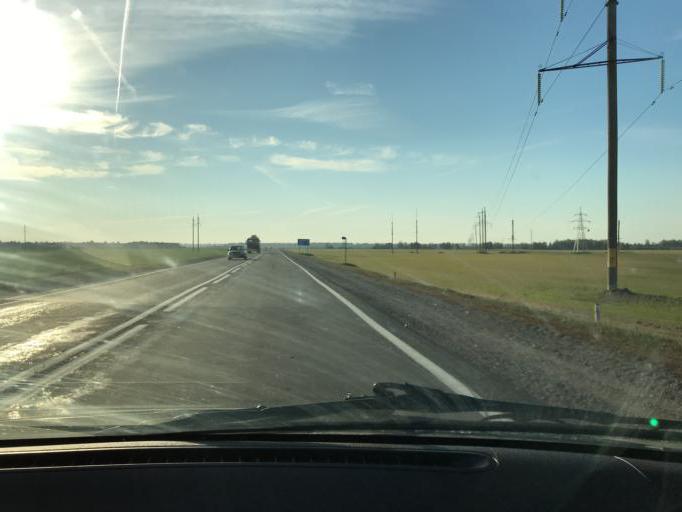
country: BY
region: Brest
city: Antopal'
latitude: 52.2183
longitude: 24.6743
